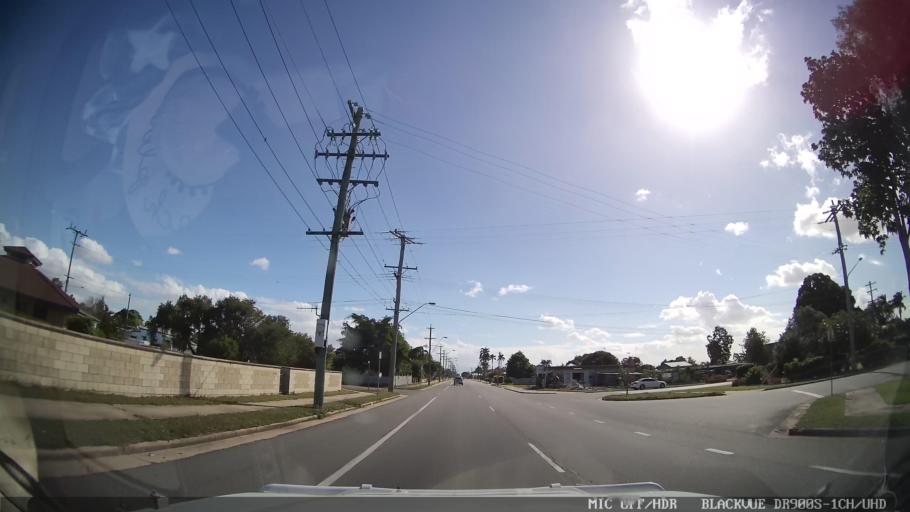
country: AU
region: Queensland
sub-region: Burdekin
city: Ayr
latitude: -19.5546
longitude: 147.3590
